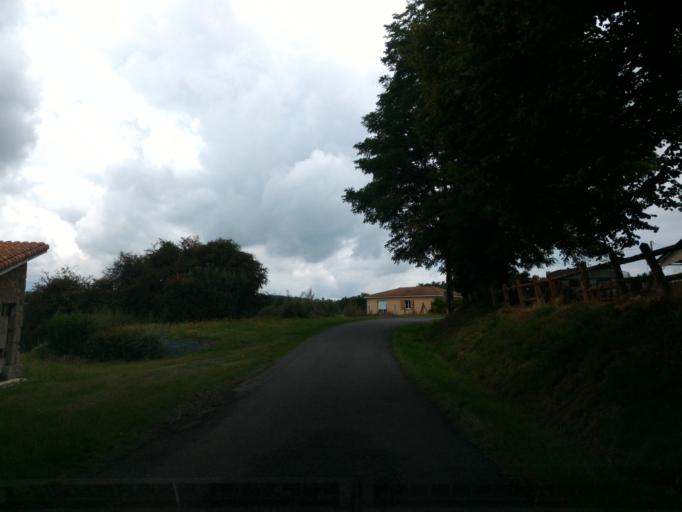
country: FR
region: Poitou-Charentes
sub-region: Departement de la Charente
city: Chabanais
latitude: 45.8920
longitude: 0.7431
